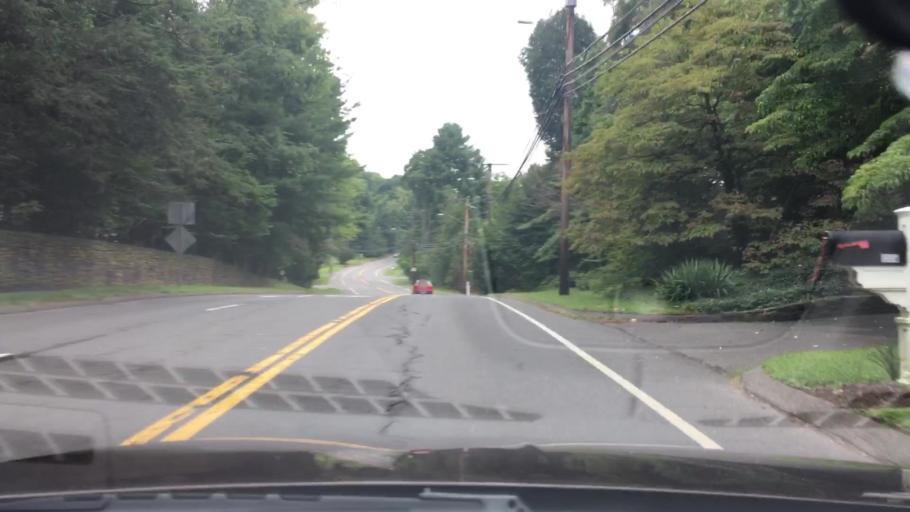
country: US
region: Connecticut
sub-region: Hartford County
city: West Hartford
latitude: 41.7667
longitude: -72.7648
